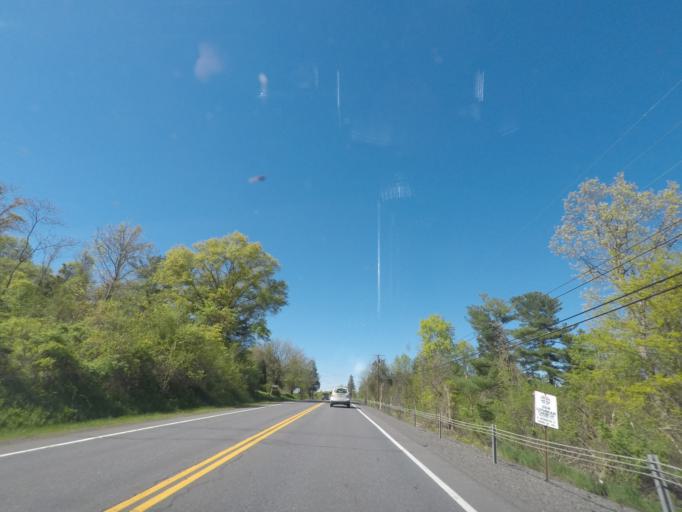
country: US
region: New York
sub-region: Greene County
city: Jefferson Heights
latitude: 42.2580
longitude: -73.8582
